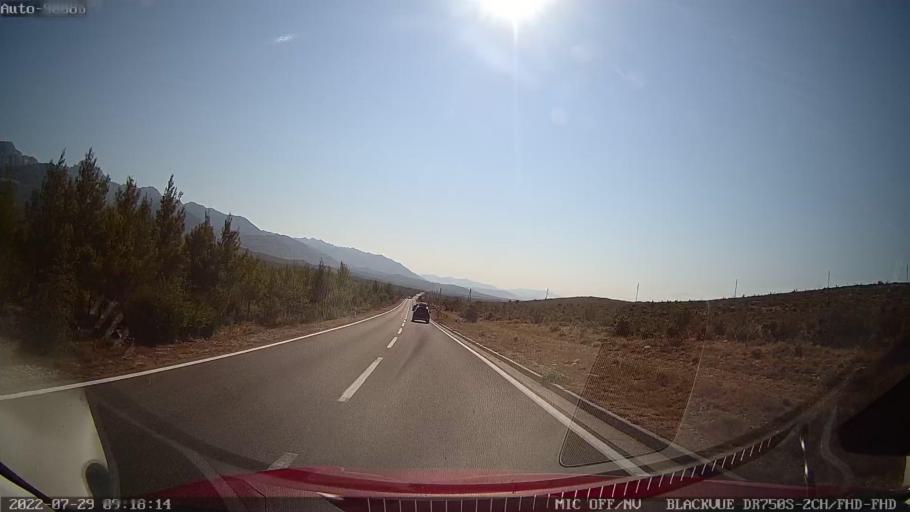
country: HR
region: Zadarska
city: Pridraga
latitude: 44.2288
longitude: 15.5967
